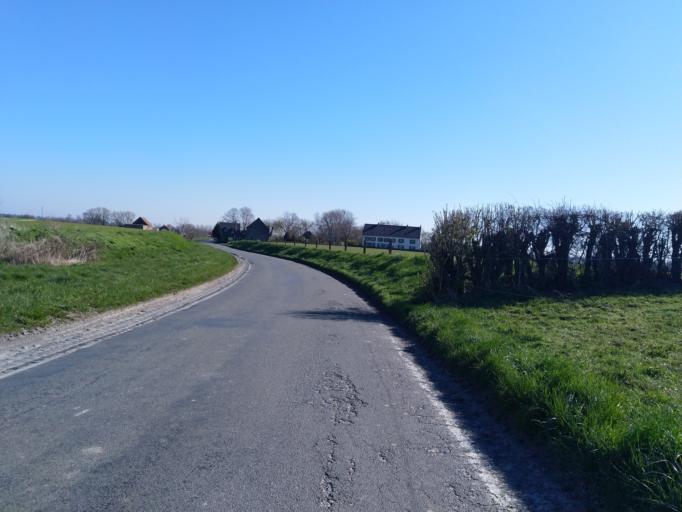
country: BE
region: Wallonia
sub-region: Province du Hainaut
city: Lens
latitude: 50.5491
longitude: 3.8701
